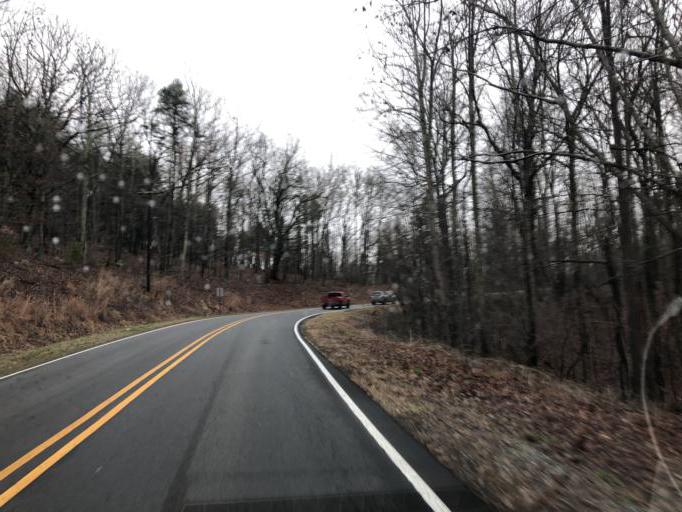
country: US
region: North Carolina
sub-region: Gaston County
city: Ranlo
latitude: 35.2971
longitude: -81.1191
